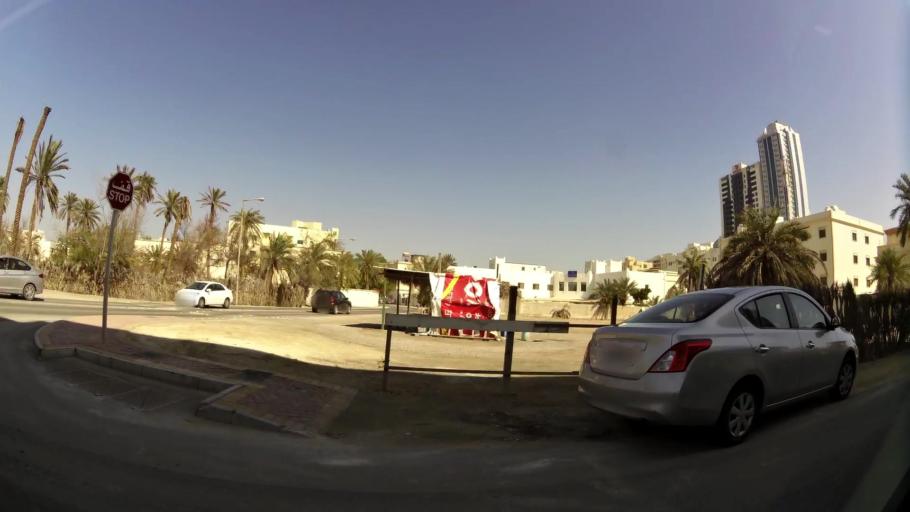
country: BH
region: Manama
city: Manama
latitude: 26.2064
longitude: 50.5773
